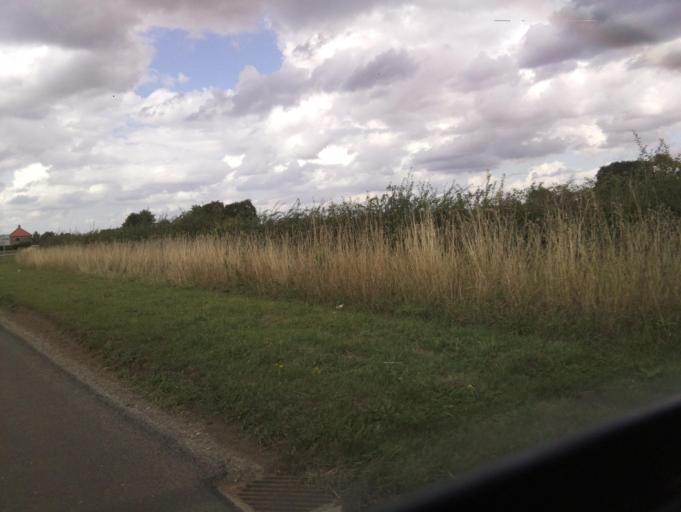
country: GB
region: England
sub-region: North Yorkshire
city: Ripon
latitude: 54.1573
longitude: -1.5410
